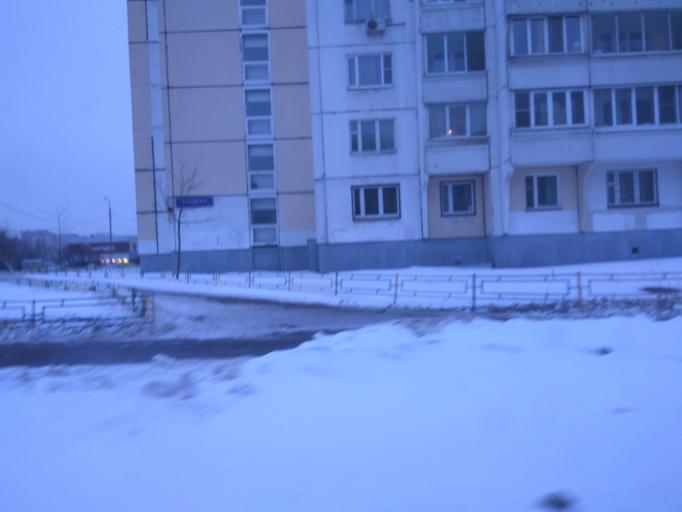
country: RU
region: Moscow
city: Gol'yanovo
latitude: 55.8137
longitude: 37.8283
